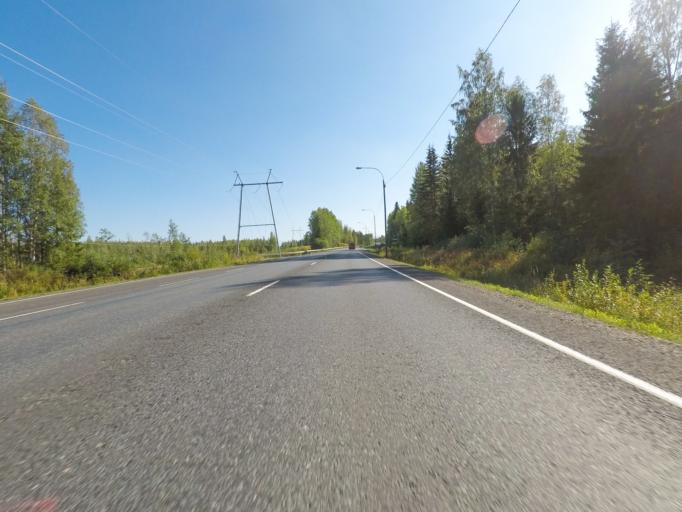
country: FI
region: Northern Savo
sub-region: Varkaus
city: Leppaevirta
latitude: 62.5752
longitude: 27.6065
